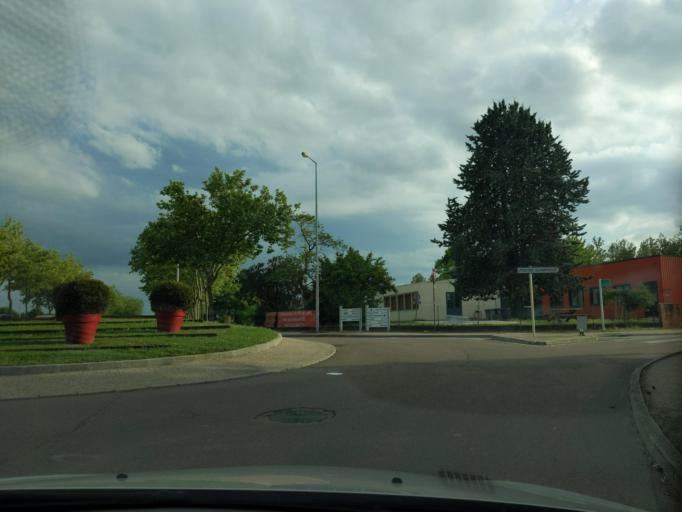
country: FR
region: Bourgogne
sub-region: Departement de la Cote-d'Or
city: Saint-Apollinaire
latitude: 47.3164
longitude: 5.0945
